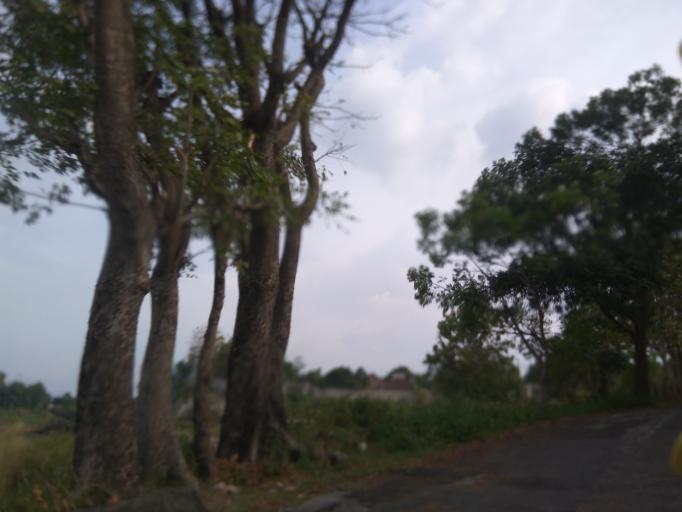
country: ID
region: Central Java
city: Semarang
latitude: -7.0265
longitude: 110.4429
